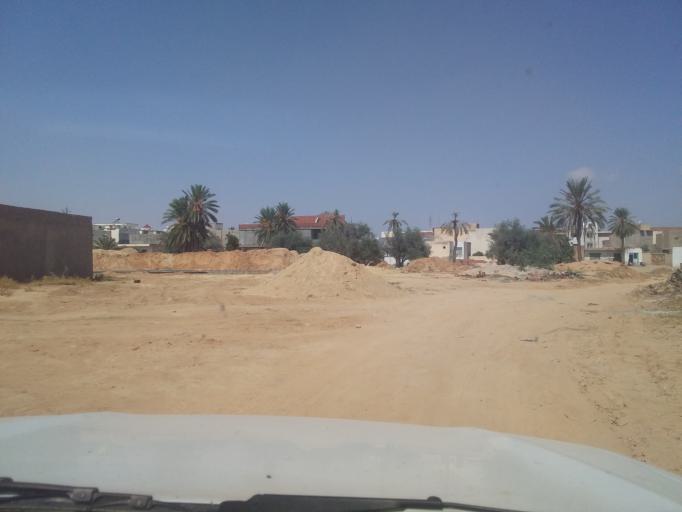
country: TN
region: Qabis
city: Matmata
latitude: 33.6165
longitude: 10.2860
